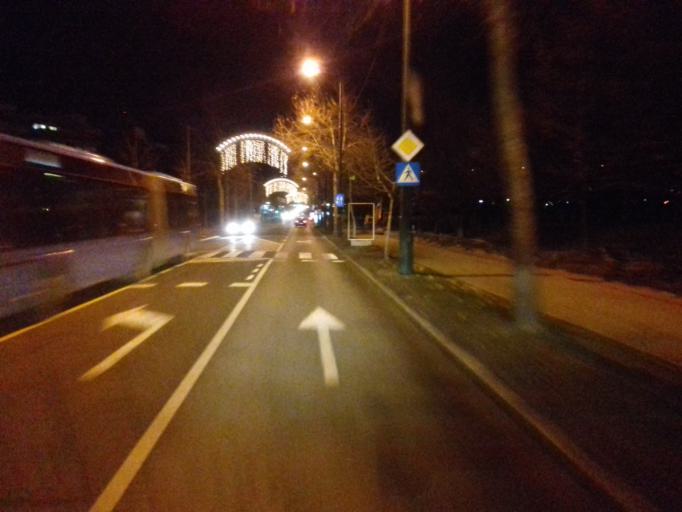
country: BA
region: Federation of Bosnia and Herzegovina
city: Kobilja Glava
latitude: 43.8651
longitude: 18.4108
